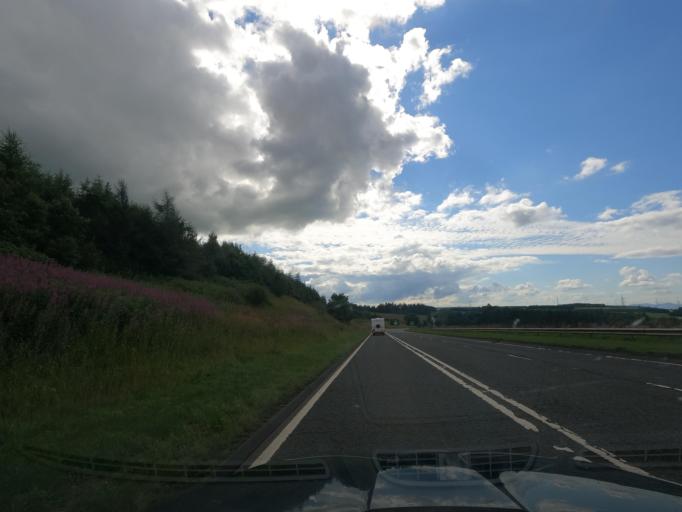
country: GB
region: Scotland
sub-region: East Lothian
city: Pencaitland
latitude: 55.8244
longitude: -2.8665
